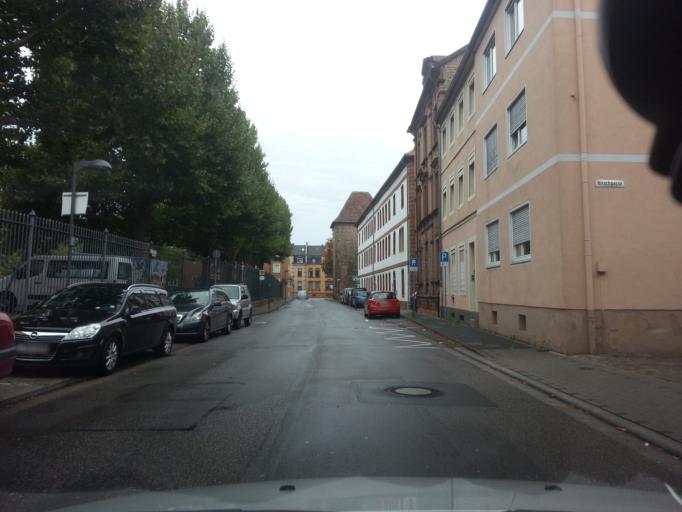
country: DE
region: Rheinland-Pfalz
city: Landau in der Pfalz
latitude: 49.1985
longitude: 8.1110
